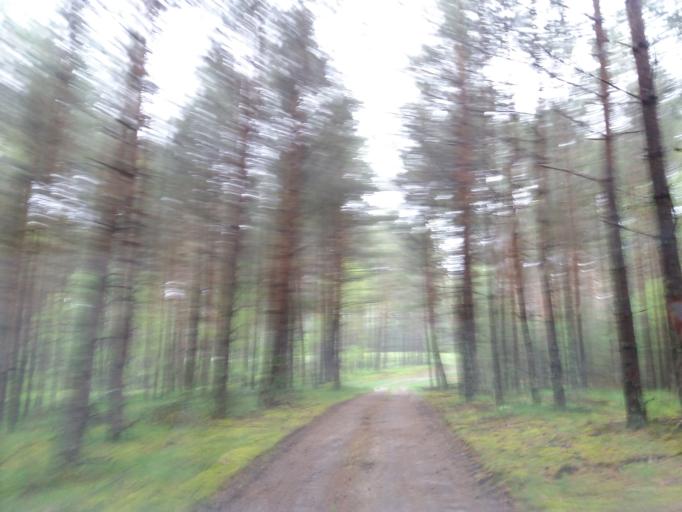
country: PL
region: West Pomeranian Voivodeship
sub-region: Powiat drawski
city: Kalisz Pomorski
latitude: 53.2417
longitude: 16.0137
